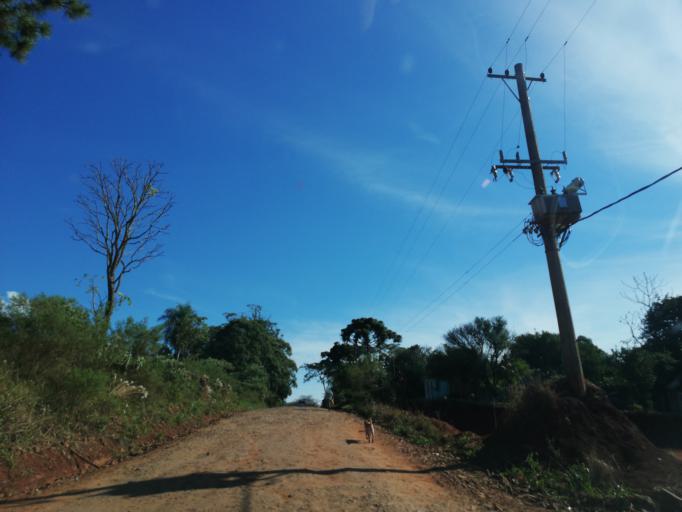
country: AR
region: Misiones
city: Dos de Mayo
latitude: -27.0175
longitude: -54.4570
